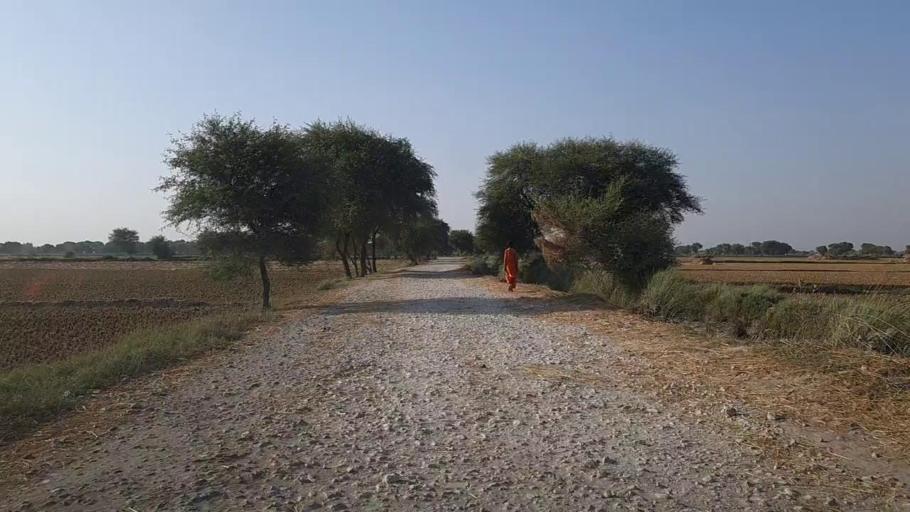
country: PK
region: Sindh
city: Kashmor
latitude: 28.4040
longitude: 69.4165
